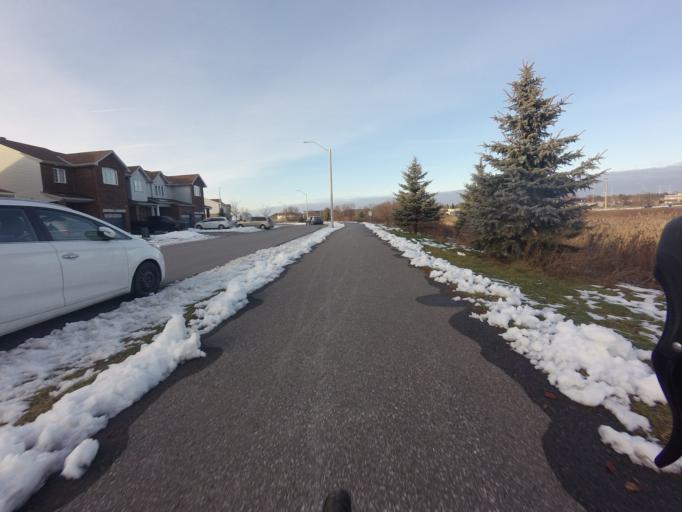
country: CA
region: Ontario
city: Bells Corners
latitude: 45.2755
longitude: -75.8622
